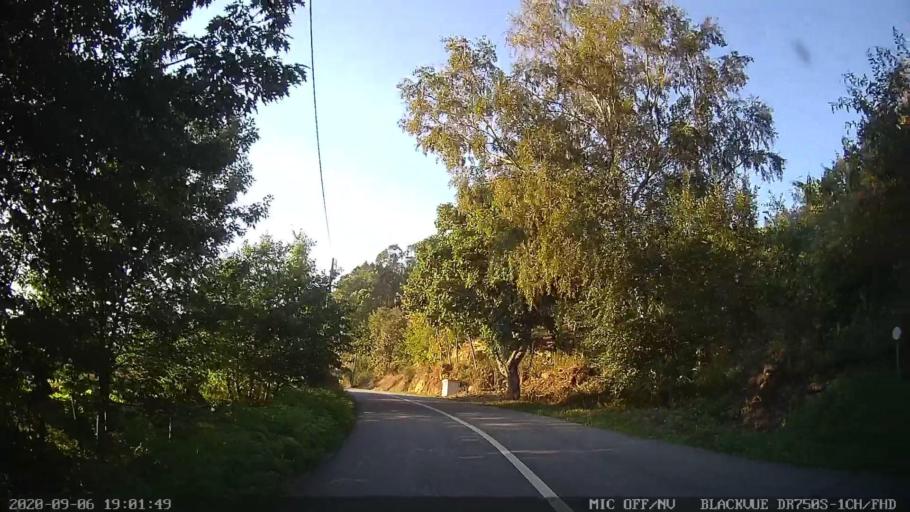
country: PT
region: Porto
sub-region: Baiao
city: Baiao
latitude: 41.2329
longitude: -7.9971
